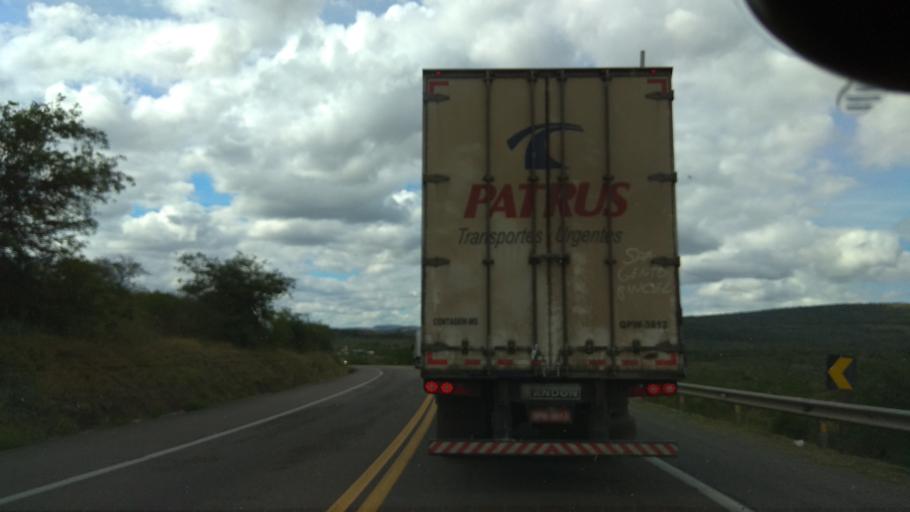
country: BR
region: Bahia
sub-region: Santa Ines
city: Santa Ines
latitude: -12.9908
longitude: -39.9472
